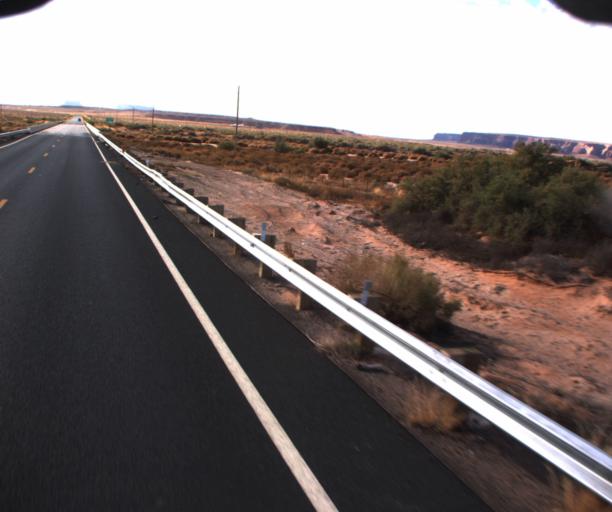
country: US
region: Arizona
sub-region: Apache County
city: Many Farms
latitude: 36.6282
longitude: -109.5842
